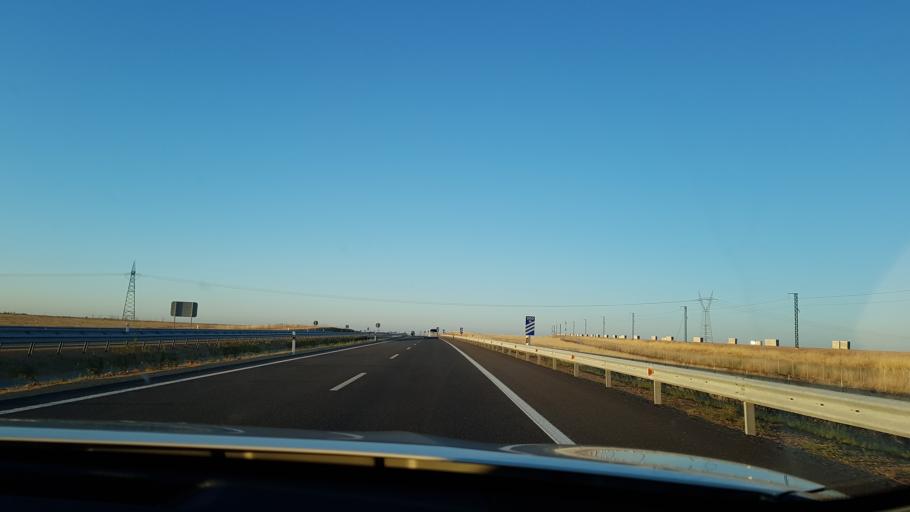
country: ES
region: Castille and Leon
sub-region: Provincia de Zamora
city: Montamarta
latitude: 41.6151
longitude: -5.7875
